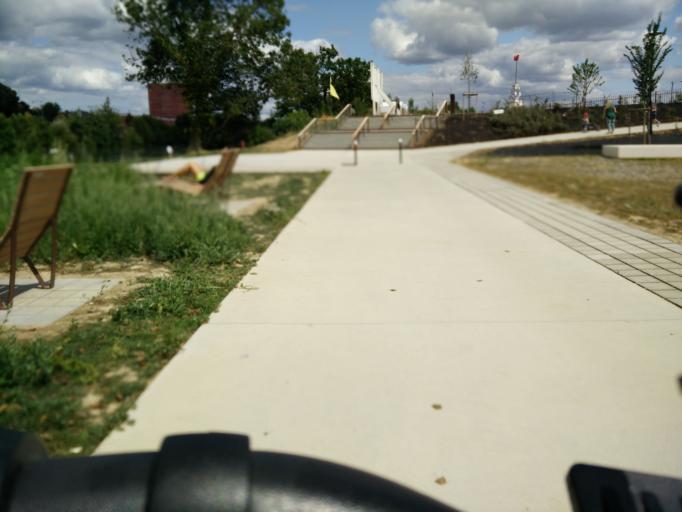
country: FR
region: Brittany
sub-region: Departement d'Ille-et-Vilaine
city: Rennes
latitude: 48.1101
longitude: -1.6489
